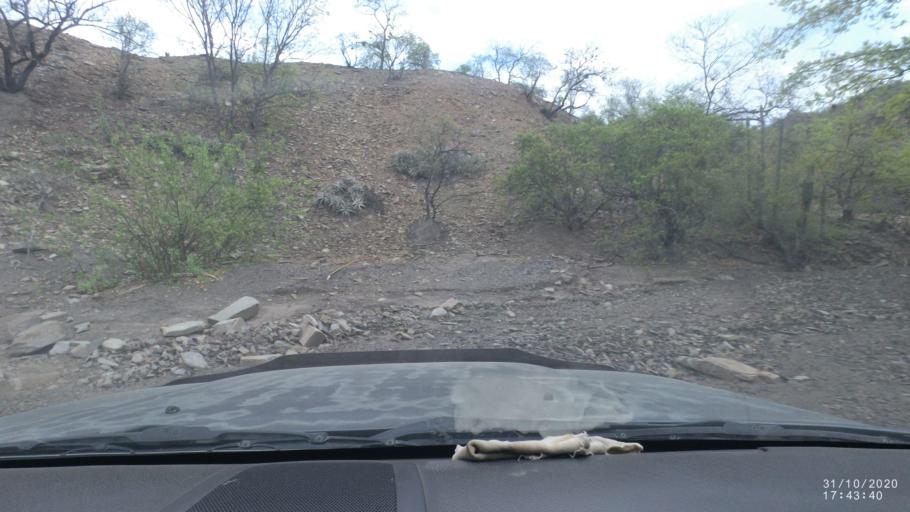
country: BO
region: Chuquisaca
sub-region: Provincia Zudanez
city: Mojocoya
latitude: -18.6093
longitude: -64.5481
